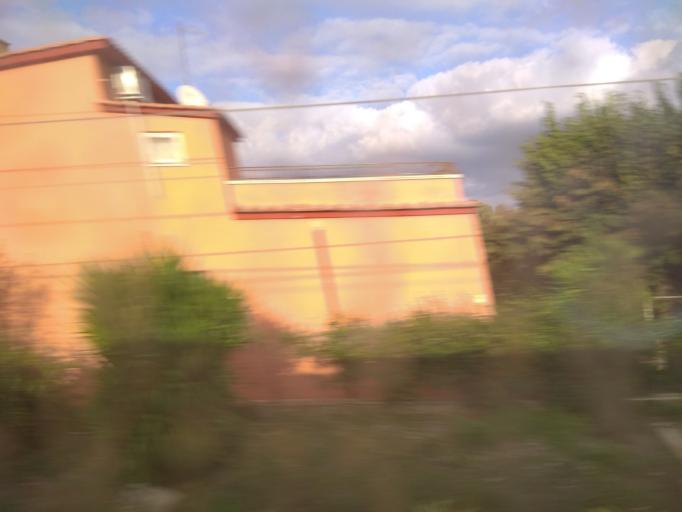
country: IT
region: Latium
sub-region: Citta metropolitana di Roma Capitale
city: Maccarese
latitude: 41.9119
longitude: 12.2041
